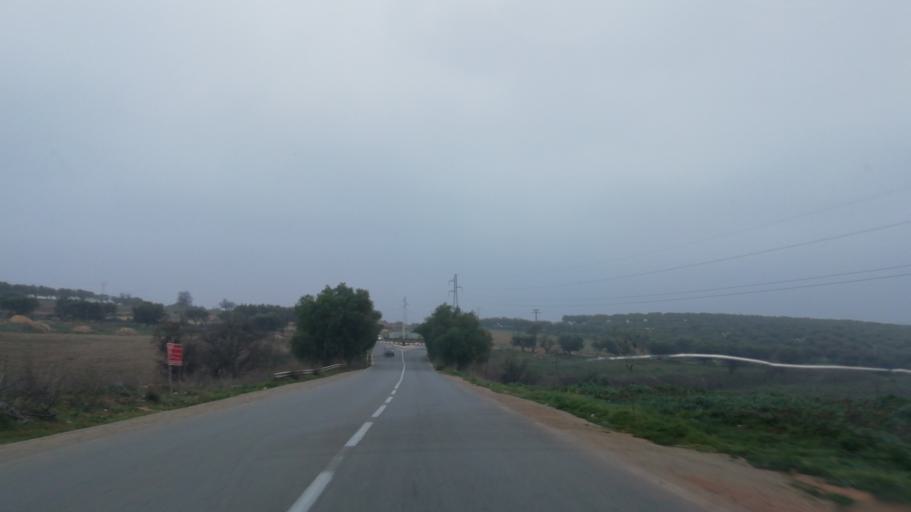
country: DZ
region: Mascara
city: Mascara
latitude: 35.4005
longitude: 0.1643
